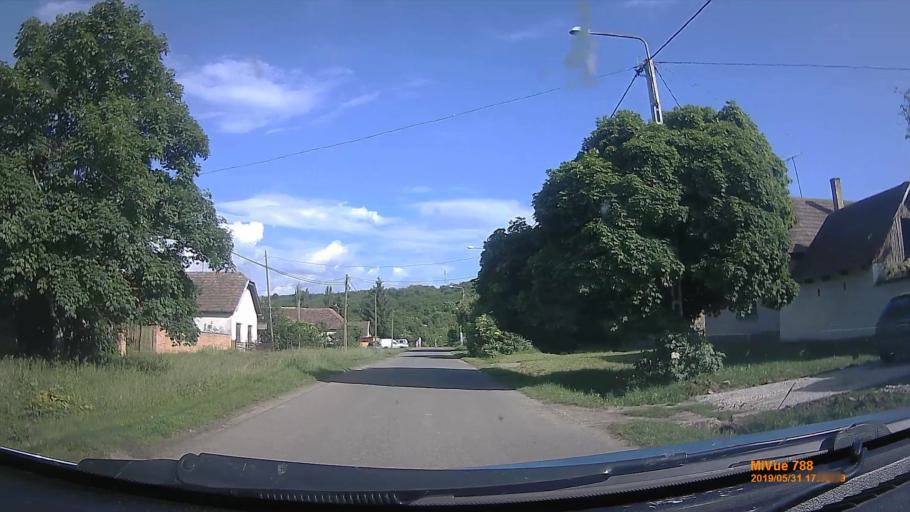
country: HU
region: Nograd
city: Nagyoroszi
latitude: 48.0444
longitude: 19.0544
